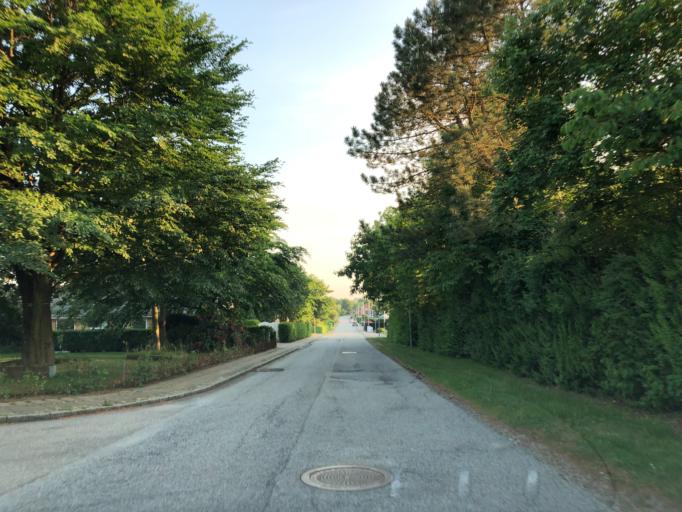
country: DK
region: Central Jutland
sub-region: Struer Kommune
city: Struer
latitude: 56.4190
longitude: 8.4926
